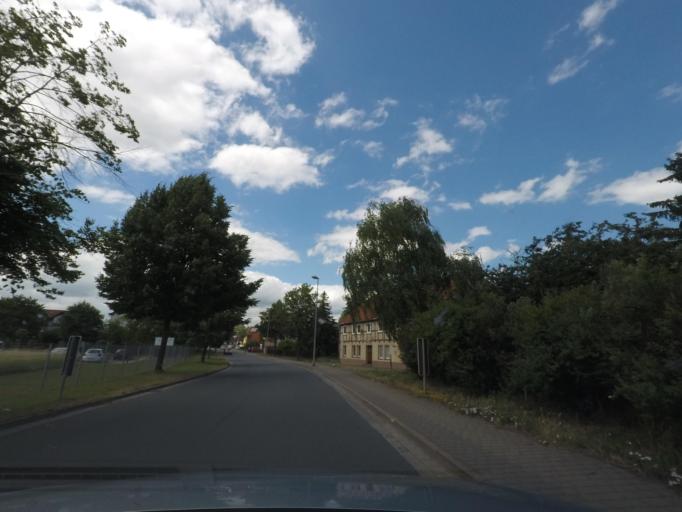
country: DE
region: Saxony-Anhalt
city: Gross Quenstedt
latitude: 51.9236
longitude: 11.1083
